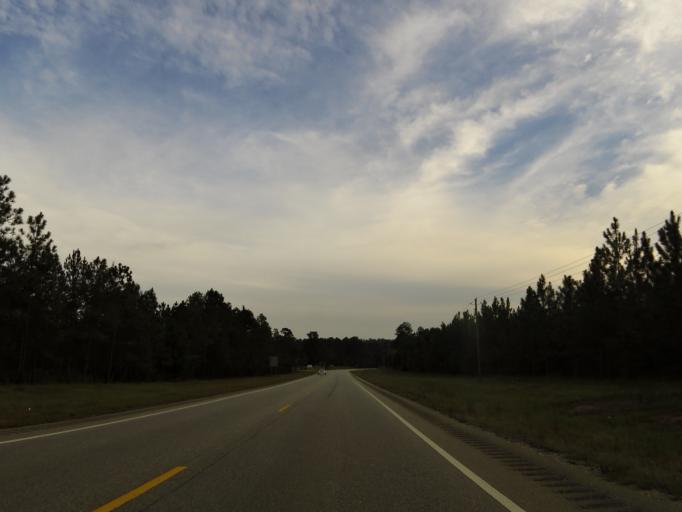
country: US
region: Alabama
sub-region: Monroe County
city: Frisco City
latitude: 31.2618
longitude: -87.4951
